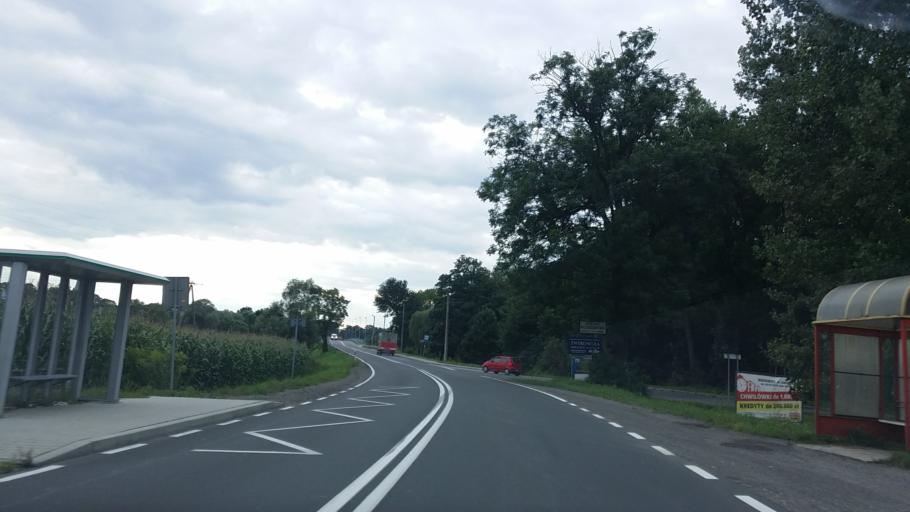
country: PL
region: Lesser Poland Voivodeship
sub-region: Powiat oswiecimski
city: Zator
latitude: 49.9995
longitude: 19.4507
